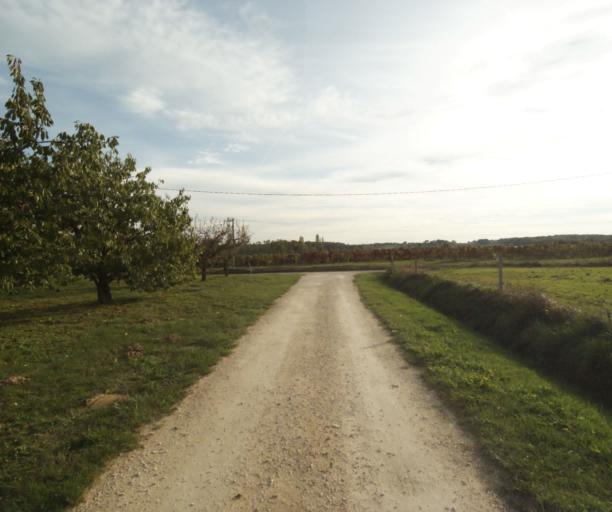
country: FR
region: Midi-Pyrenees
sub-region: Departement du Tarn-et-Garonne
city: Campsas
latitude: 43.8813
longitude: 1.3430
